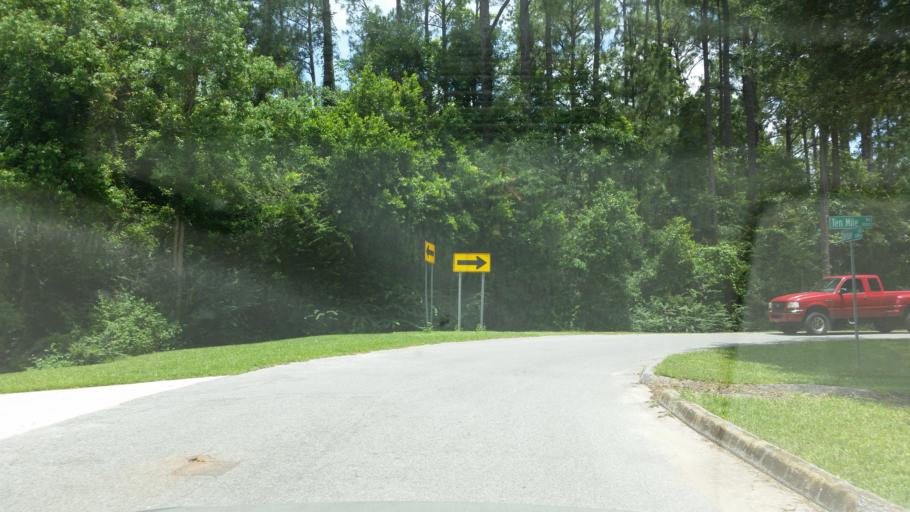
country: US
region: Florida
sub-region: Escambia County
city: Gonzalez
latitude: 30.5483
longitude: -87.3021
